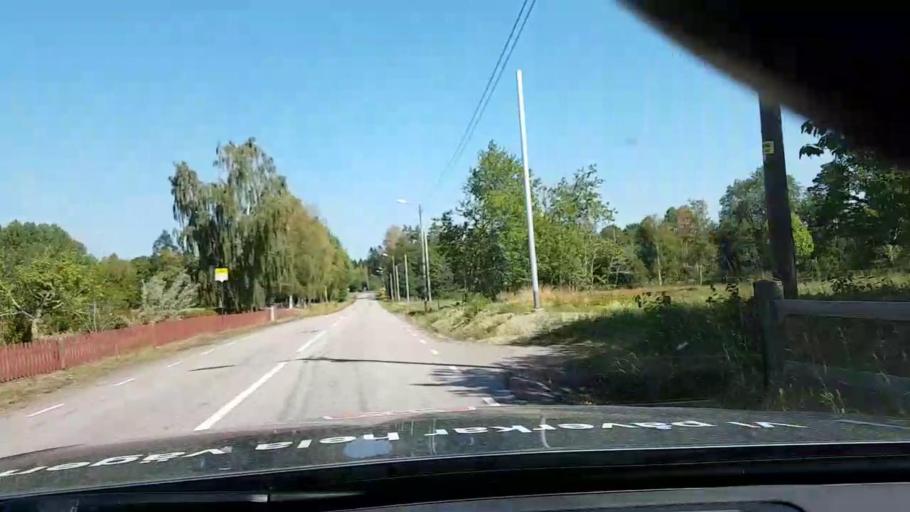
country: SE
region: Kalmar
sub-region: Hultsfreds Kommun
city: Virserum
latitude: 57.1363
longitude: 15.6597
